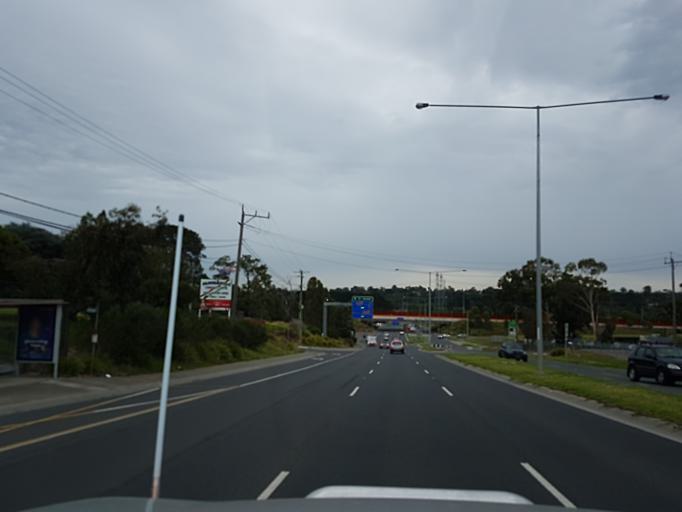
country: AU
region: Victoria
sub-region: Knox
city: Wantirna
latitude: -37.8468
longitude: 145.2209
